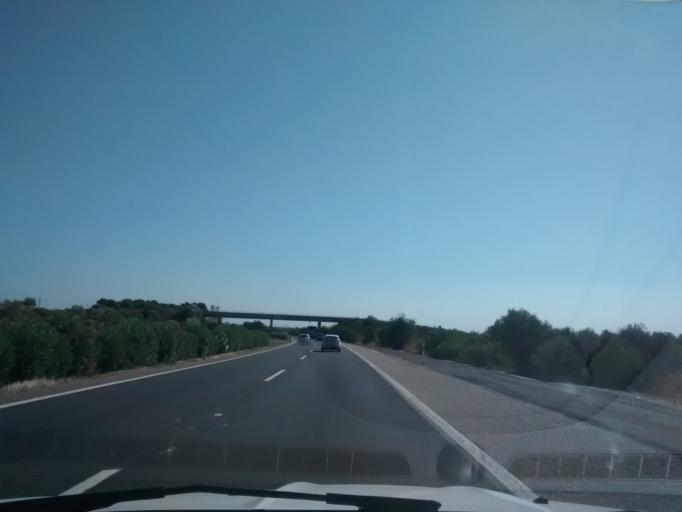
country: ES
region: Balearic Islands
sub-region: Illes Balears
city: Binissalem
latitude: 39.6824
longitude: 2.8545
